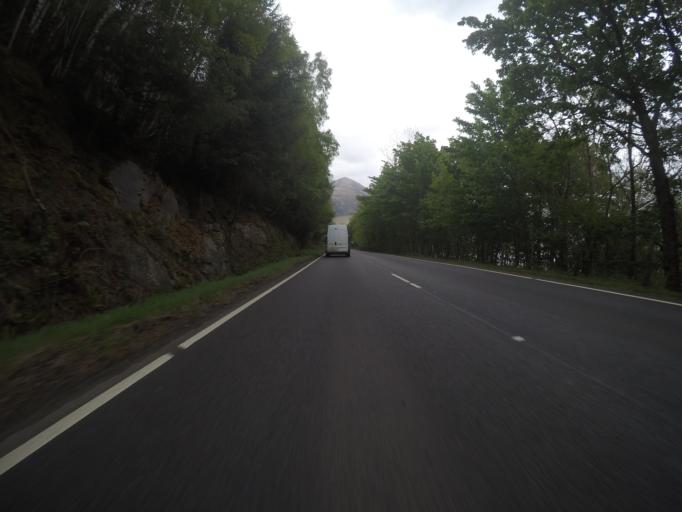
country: GB
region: Scotland
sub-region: Highland
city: Fort William
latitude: 57.2355
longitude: -5.4308
